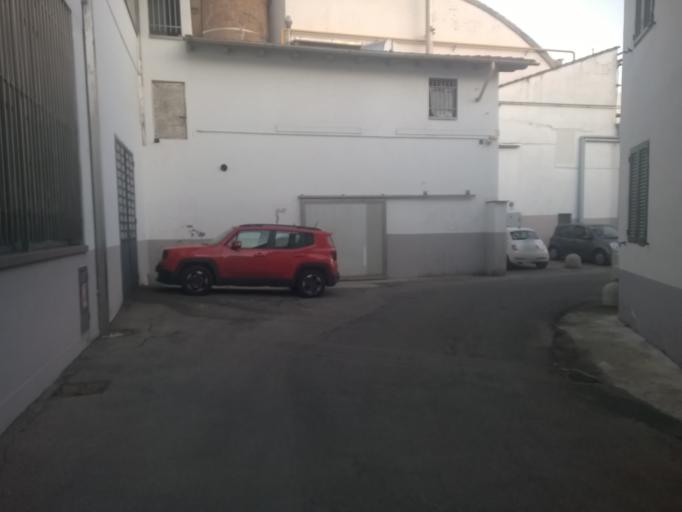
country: IT
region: Tuscany
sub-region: Provincia di Prato
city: Prato
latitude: 43.8704
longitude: 11.1010
